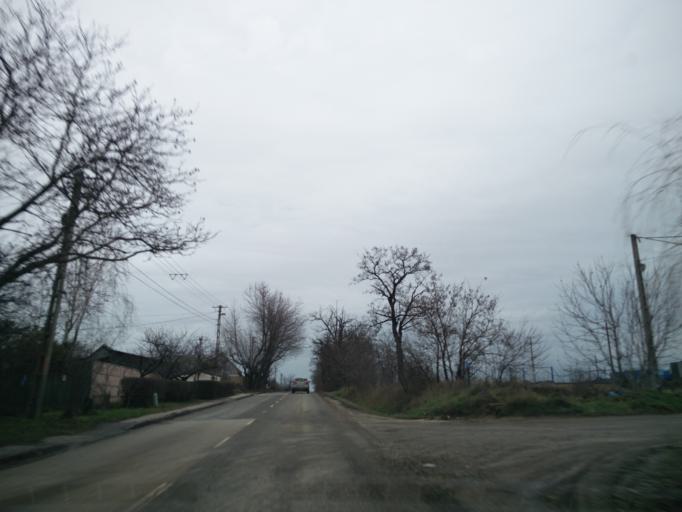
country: HU
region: Pest
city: Gyomro
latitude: 47.4236
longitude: 19.4142
